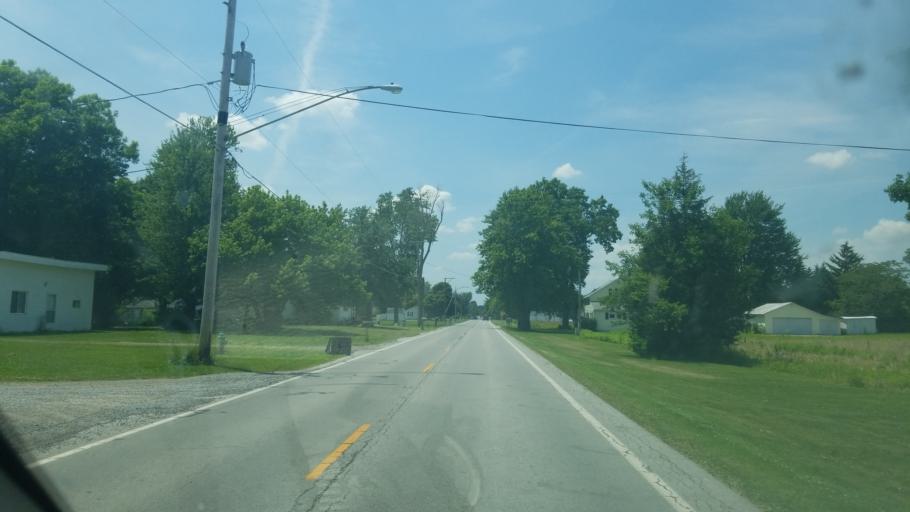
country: US
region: Ohio
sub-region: Hardin County
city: Ada
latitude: 40.7767
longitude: -83.8146
